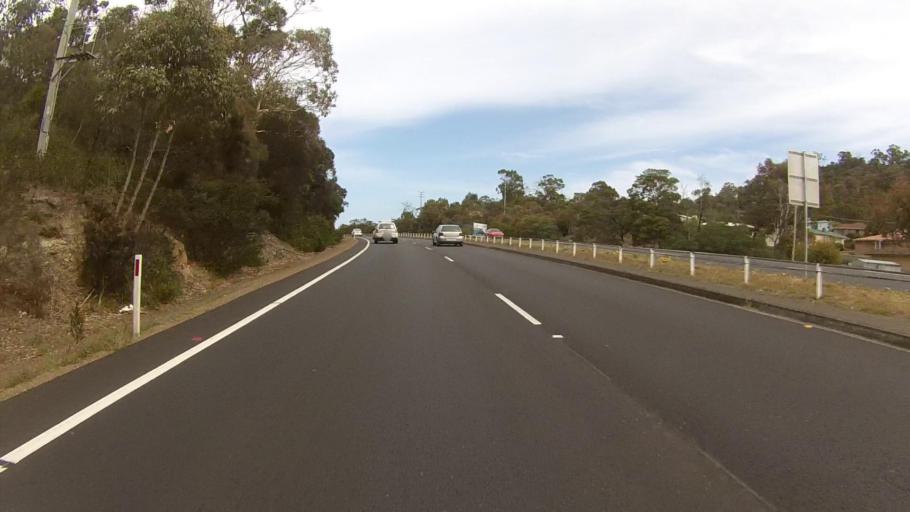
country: AU
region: Tasmania
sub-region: Clarence
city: Warrane
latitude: -42.8634
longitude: 147.3932
